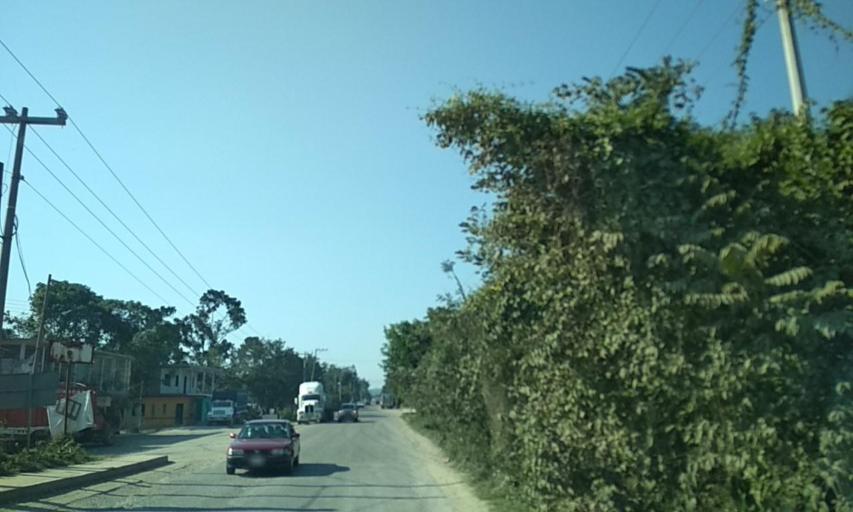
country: MX
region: Veracruz
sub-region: Papantla
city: El Chote
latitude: 20.4032
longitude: -97.3412
